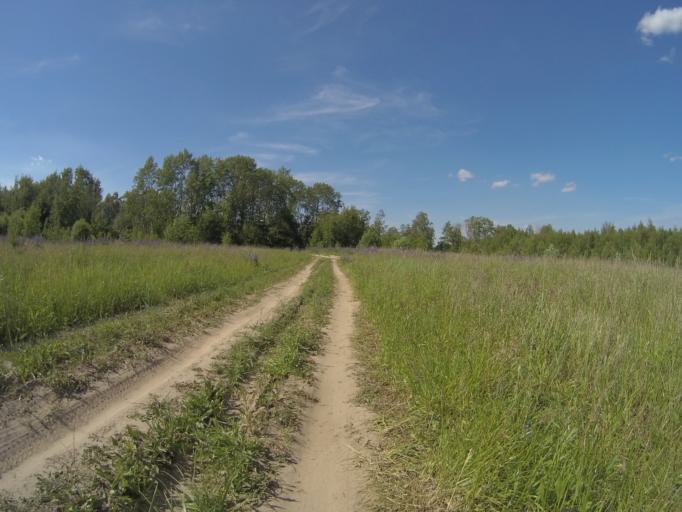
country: RU
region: Vladimir
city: Raduzhnyy
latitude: 55.9857
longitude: 40.3765
